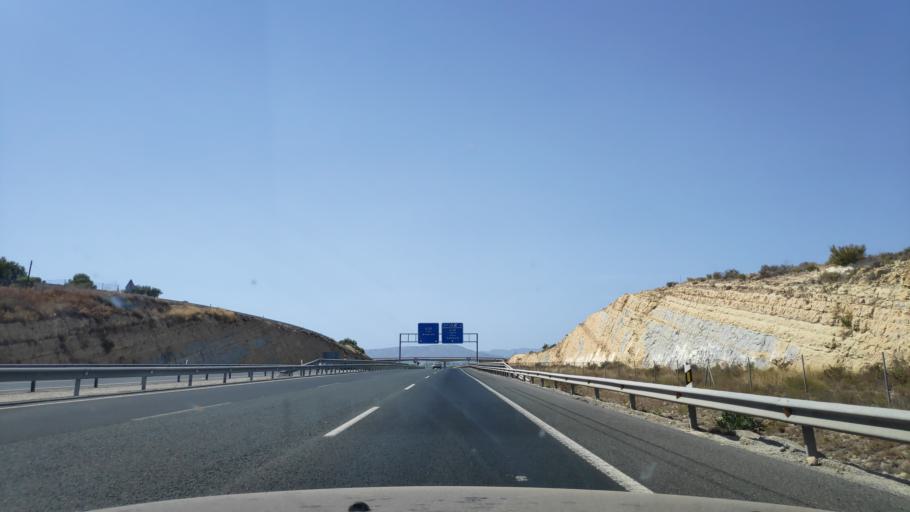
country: ES
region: Murcia
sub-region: Murcia
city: Ulea
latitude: 38.1768
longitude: -1.3141
